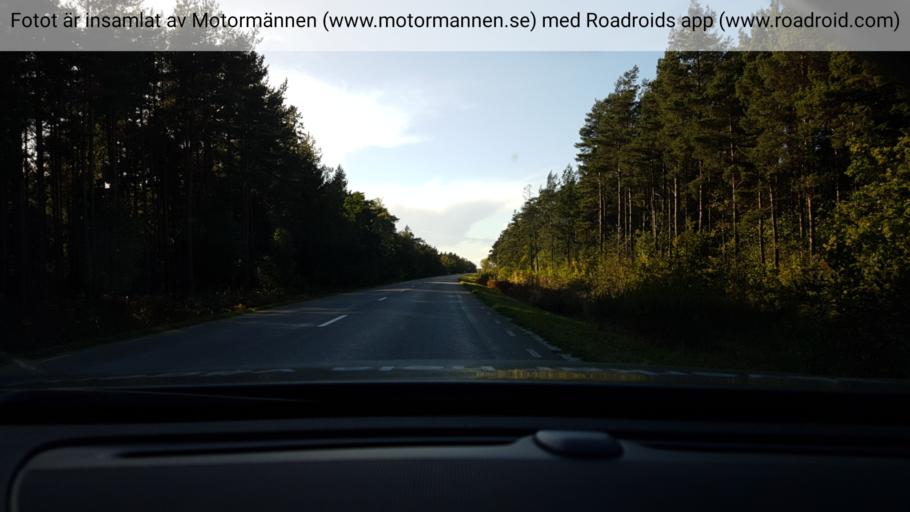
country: SE
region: Gotland
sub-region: Gotland
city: Klintehamn
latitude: 57.3800
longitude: 18.2138
